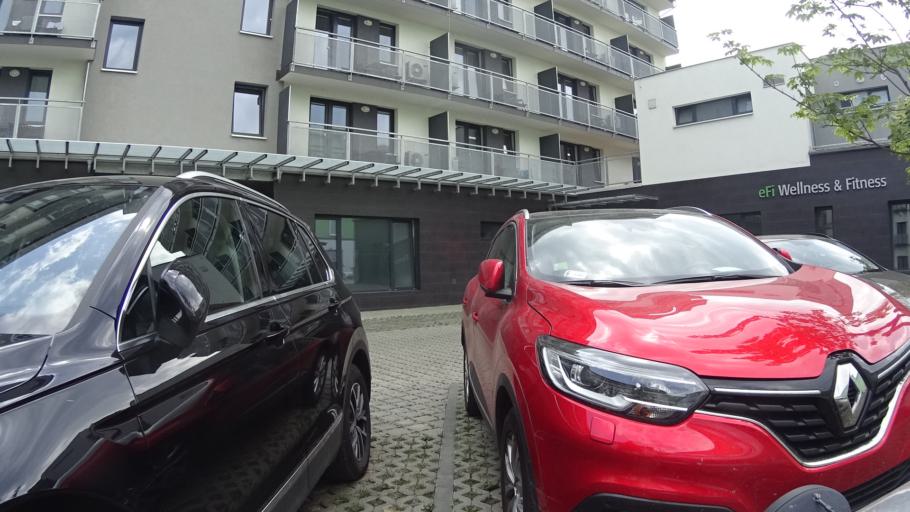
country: CZ
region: South Moravian
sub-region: Mesto Brno
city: Brno
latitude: 49.1991
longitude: 16.6199
